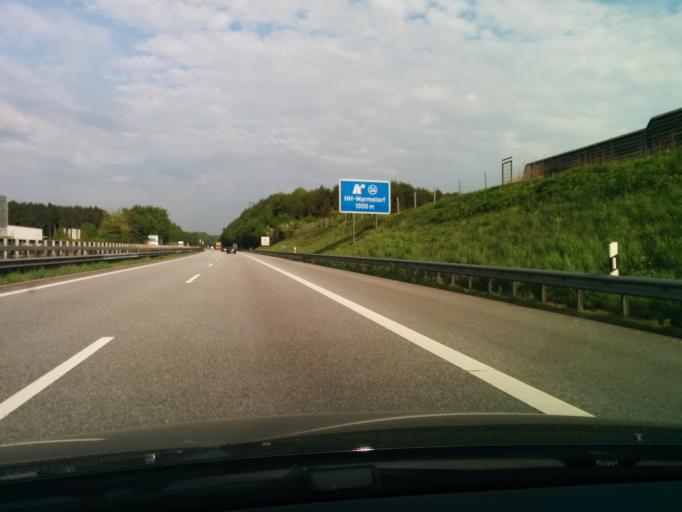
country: DE
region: Lower Saxony
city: Seevetal
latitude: 53.4281
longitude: 9.9534
